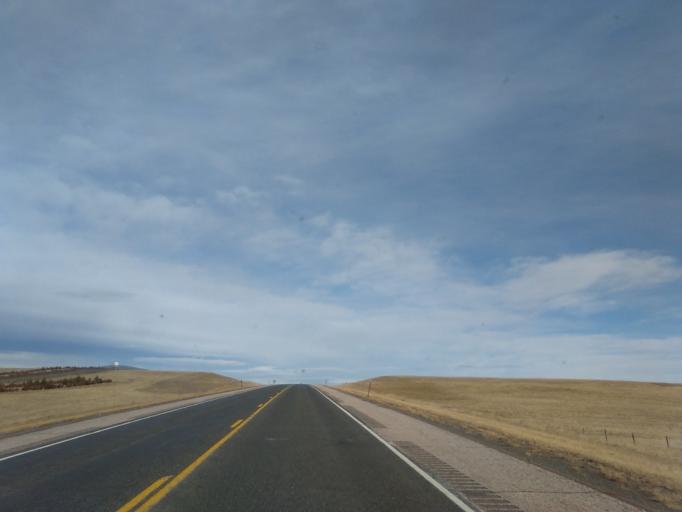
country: US
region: Wyoming
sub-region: Laramie County
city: Pine Bluffs
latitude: 41.5918
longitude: -104.2668
